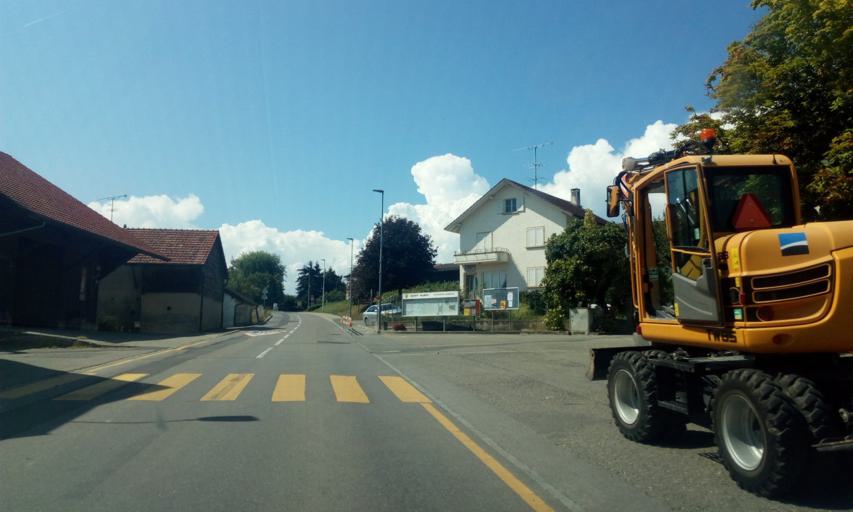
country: CH
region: Fribourg
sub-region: Broye District
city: Domdidier
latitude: 46.8899
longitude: 6.9802
